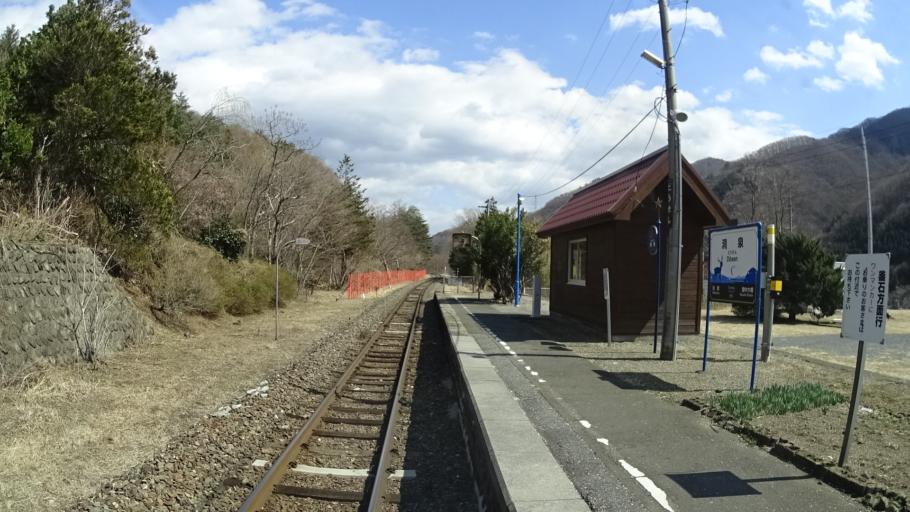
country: JP
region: Iwate
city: Kamaishi
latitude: 39.2506
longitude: 141.7605
